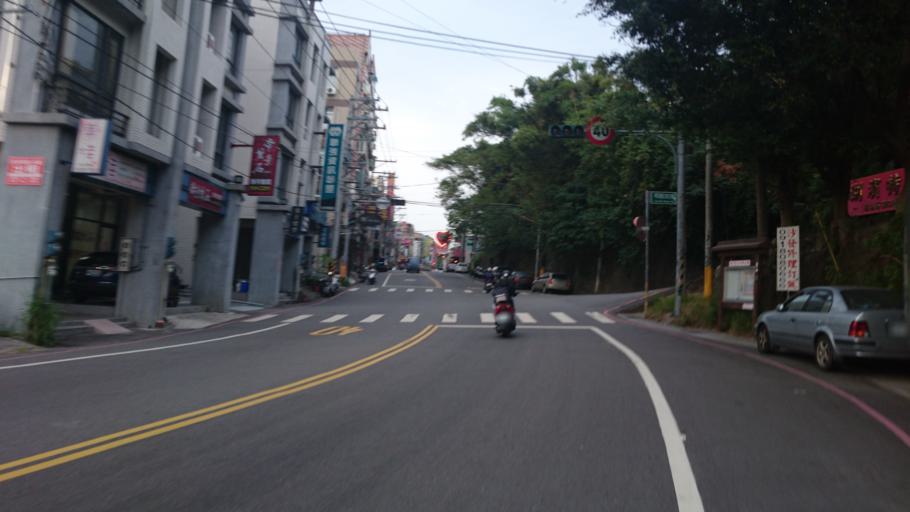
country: TW
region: Taiwan
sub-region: Hsinchu
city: Hsinchu
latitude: 24.7834
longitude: 120.9675
